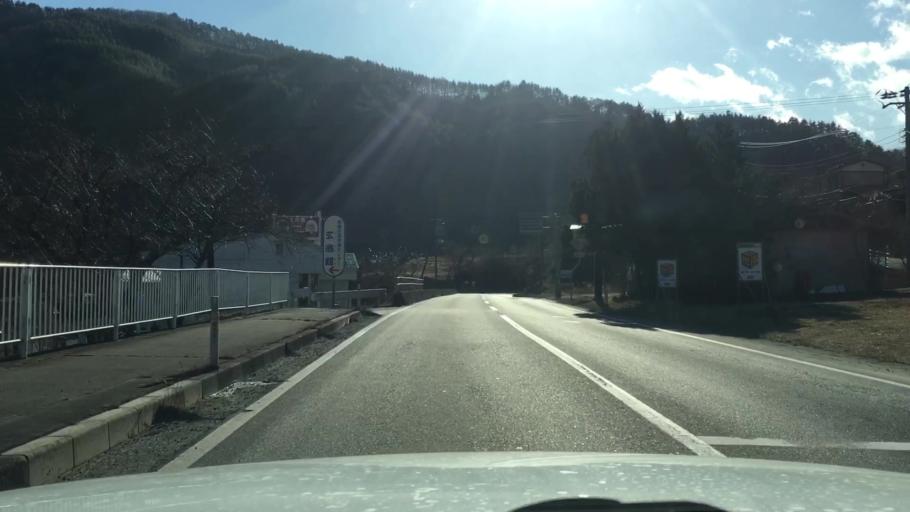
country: JP
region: Iwate
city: Miyako
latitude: 39.6173
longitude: 141.7996
